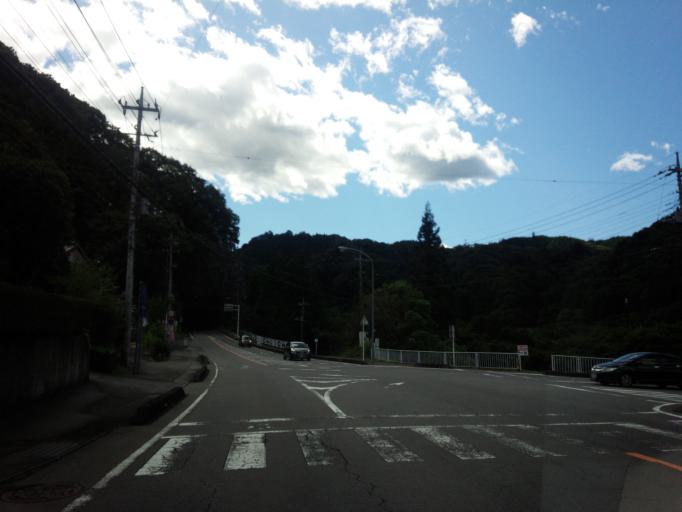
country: JP
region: Gunma
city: Nakanojomachi
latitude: 36.6081
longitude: 138.7950
